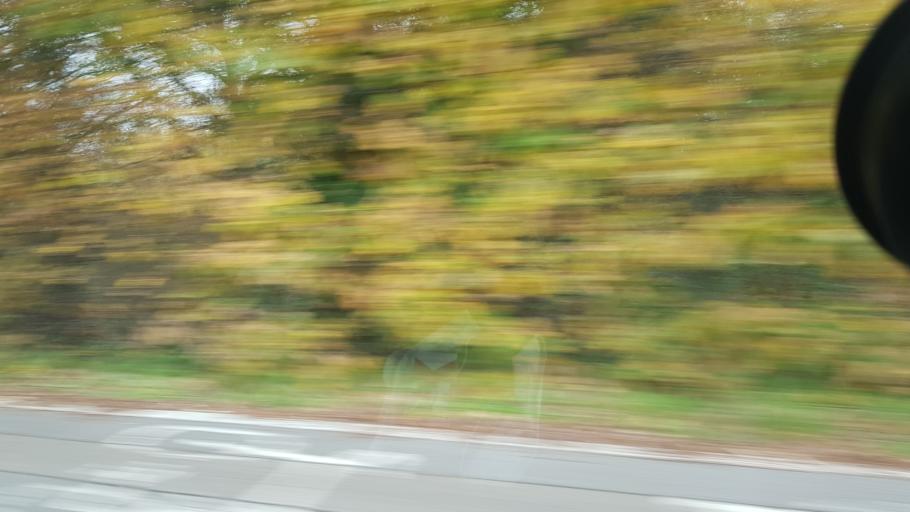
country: GB
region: England
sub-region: Hampshire
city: Farnborough
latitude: 51.2846
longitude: -0.7732
